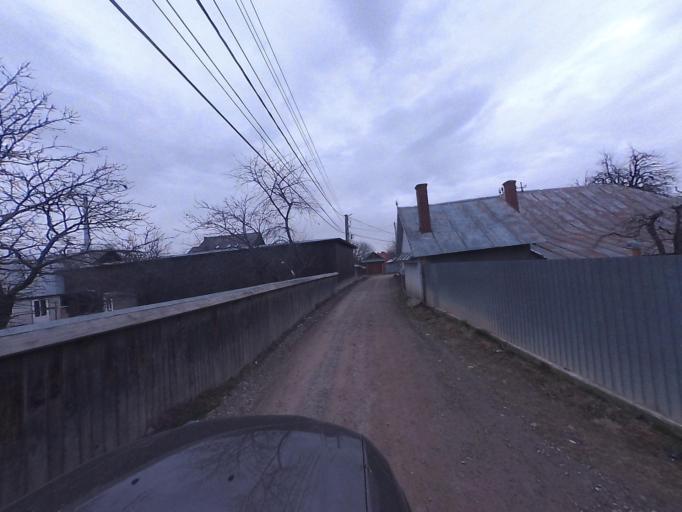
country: RO
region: Neamt
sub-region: Oras Targu Neamt
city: Humulesti
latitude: 47.1965
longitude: 26.3394
